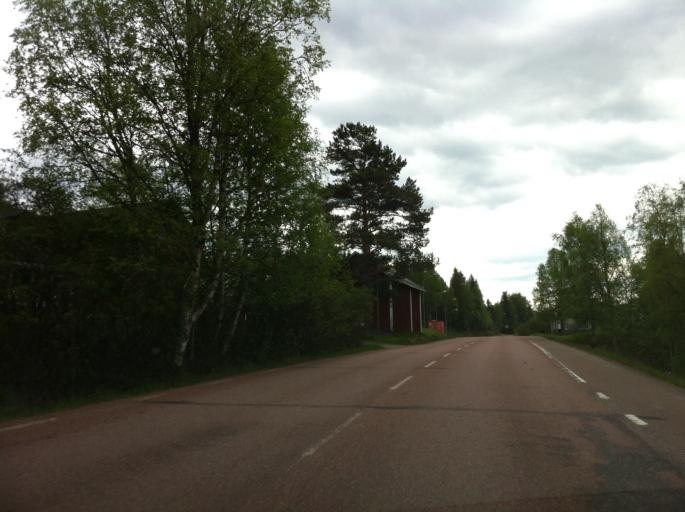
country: SE
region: Dalarna
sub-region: Malung-Saelens kommun
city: Malung
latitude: 61.0927
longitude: 13.3189
